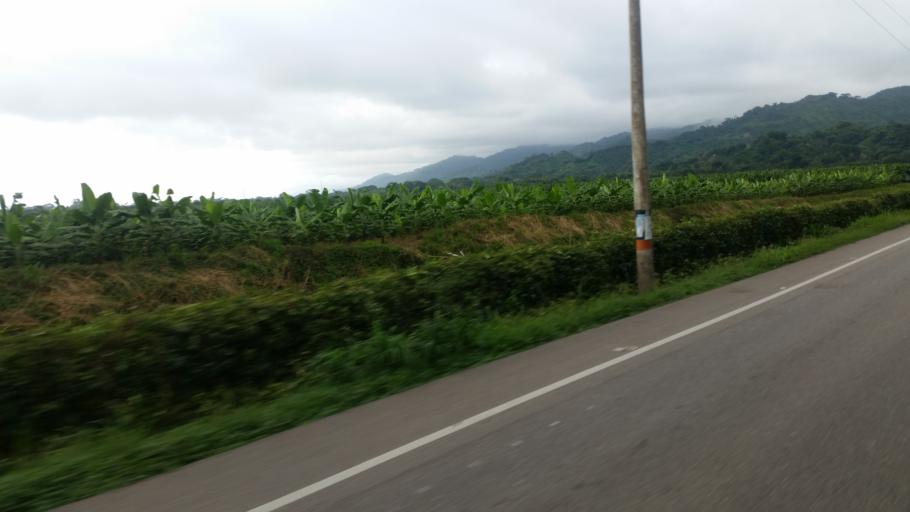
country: CO
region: Magdalena
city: Santa Marta
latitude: 11.2543
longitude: -73.8442
